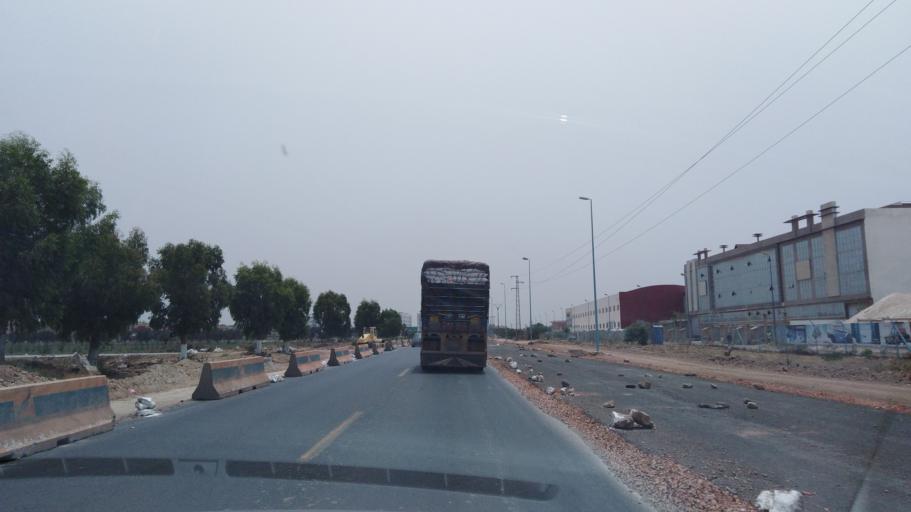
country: MA
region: Grand Casablanca
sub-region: Mediouna
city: Mediouna
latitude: 33.3936
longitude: -7.5352
